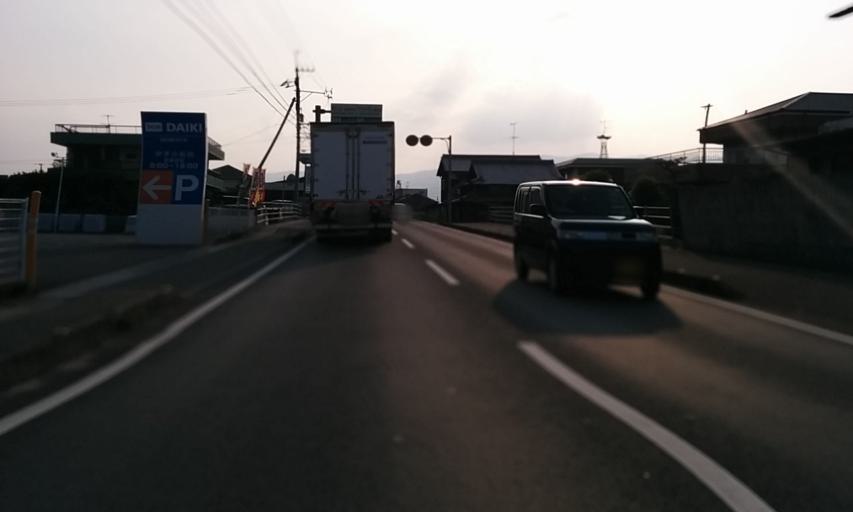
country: JP
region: Ehime
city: Saijo
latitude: 33.8959
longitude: 133.1008
